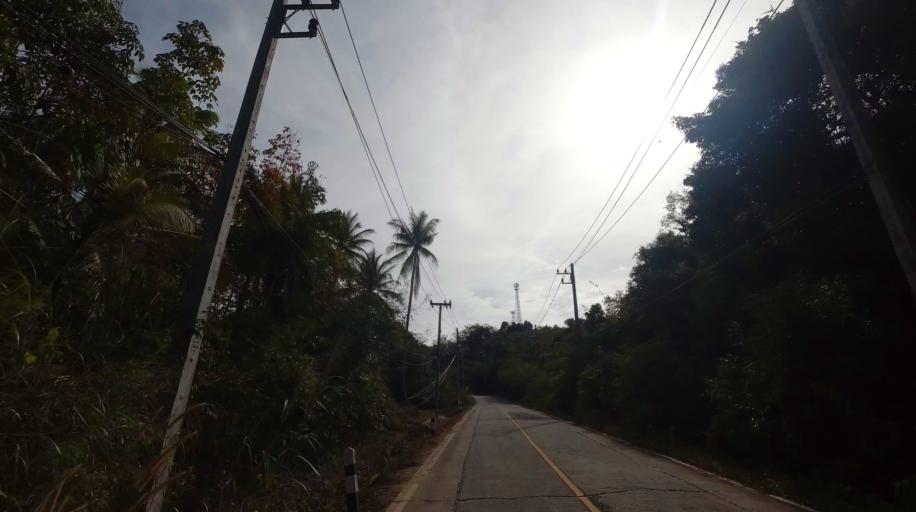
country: TH
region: Trat
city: Ko Kut
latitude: 11.6168
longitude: 102.5438
